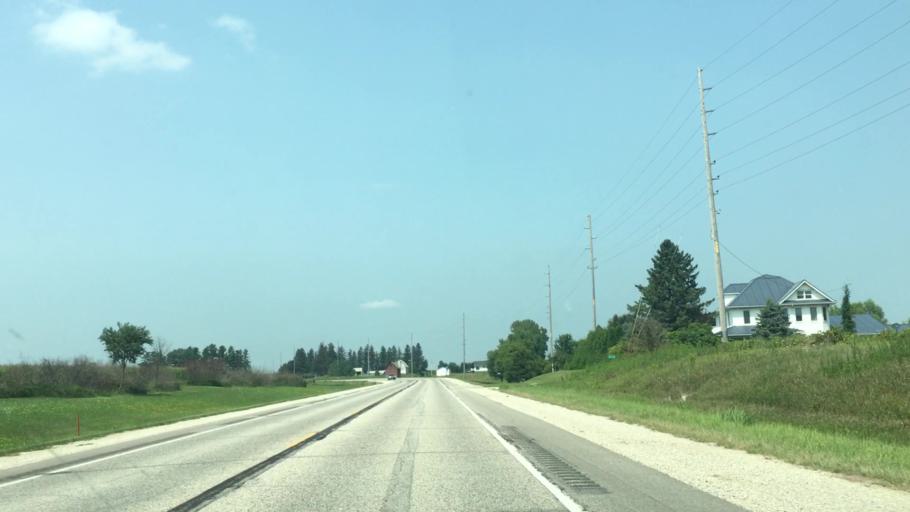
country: US
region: Iowa
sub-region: Fayette County
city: Fayette
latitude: 42.9018
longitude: -91.8105
